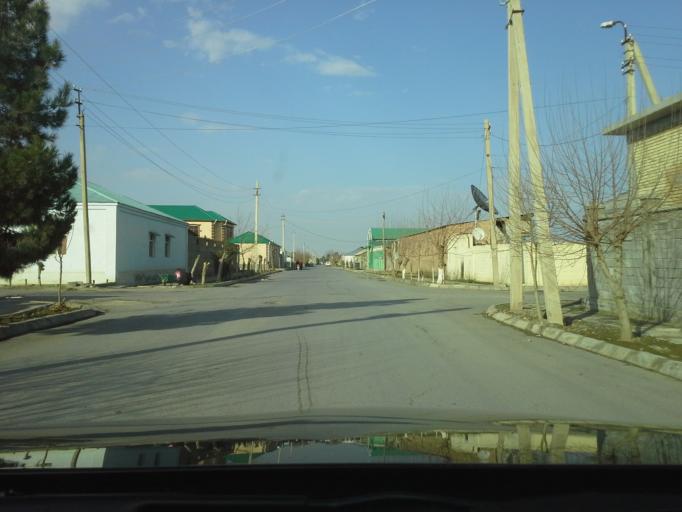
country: TM
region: Ahal
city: Abadan
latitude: 38.0205
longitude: 58.2317
